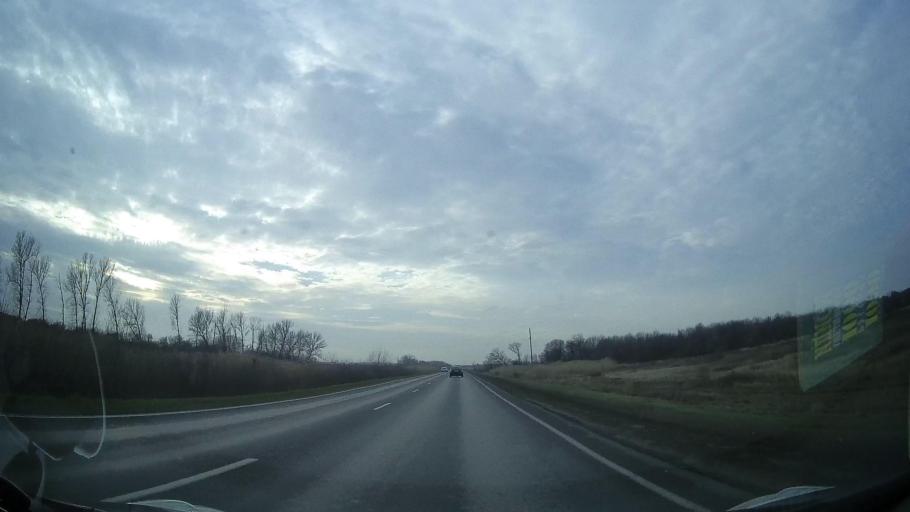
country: RU
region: Rostov
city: Starocherkasskaya
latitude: 47.1399
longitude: 40.0650
